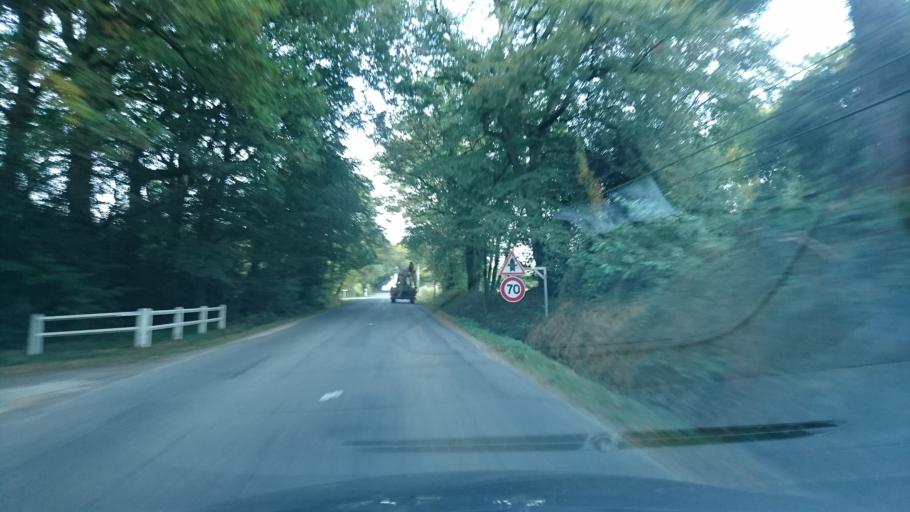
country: FR
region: Brittany
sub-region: Departement d'Ille-et-Vilaine
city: Bains-sur-Oust
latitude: 47.7318
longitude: -2.0504
